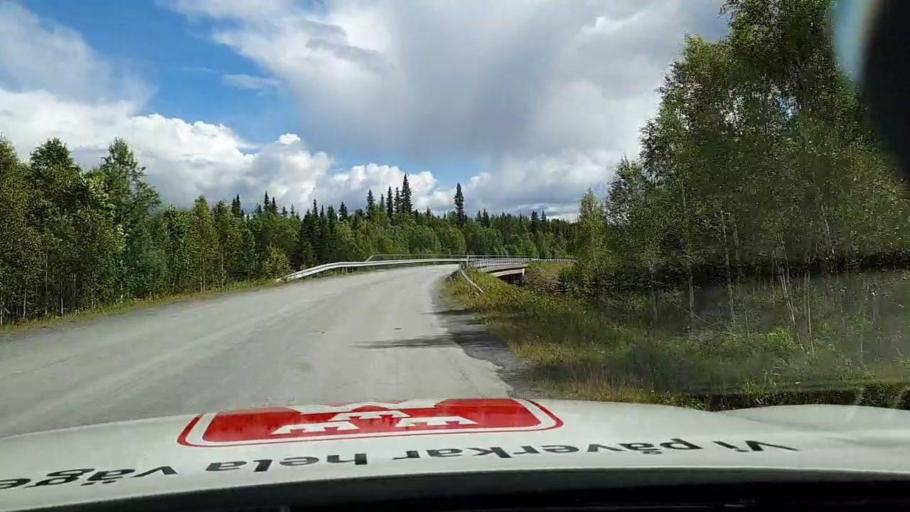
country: SE
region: Jaemtland
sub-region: Krokoms Kommun
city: Valla
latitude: 63.6865
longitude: 13.6822
